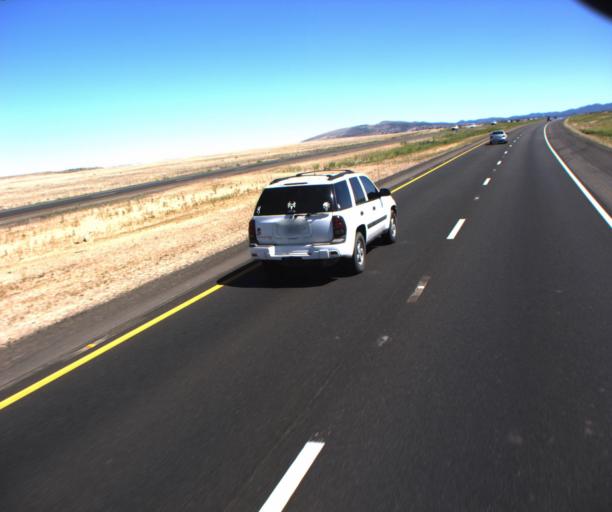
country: US
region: Arizona
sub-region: Yavapai County
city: Chino Valley
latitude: 34.6758
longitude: -112.4419
